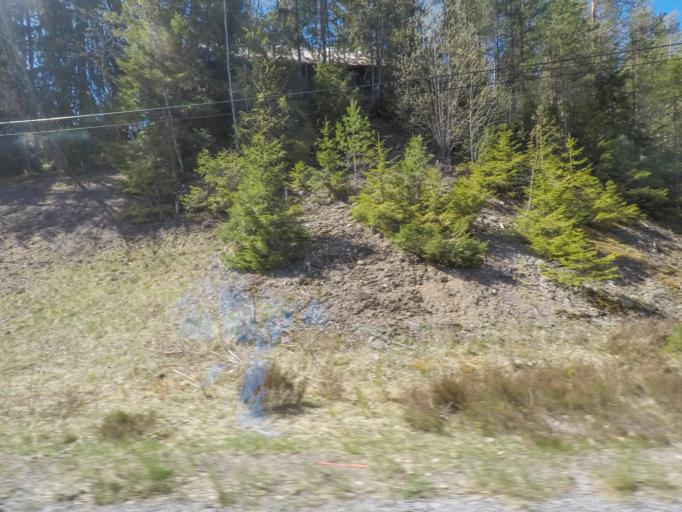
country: FI
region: Uusimaa
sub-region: Helsinki
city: Sammatti
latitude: 60.3686
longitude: 23.8099
